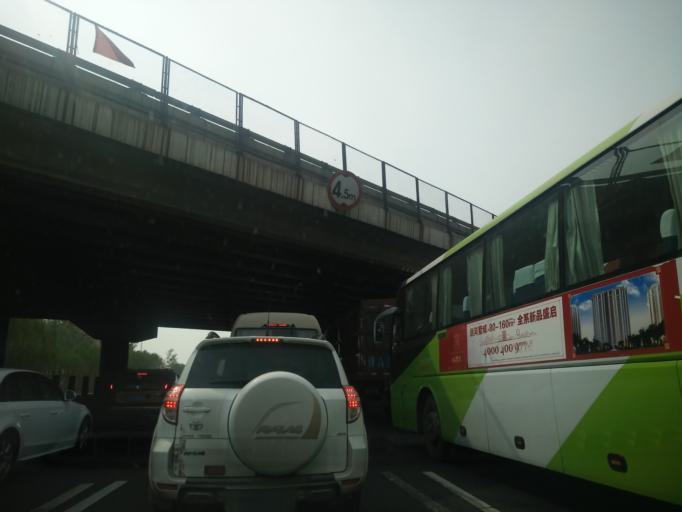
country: CN
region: Beijing
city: Xiji
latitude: 39.7988
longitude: 116.9063
